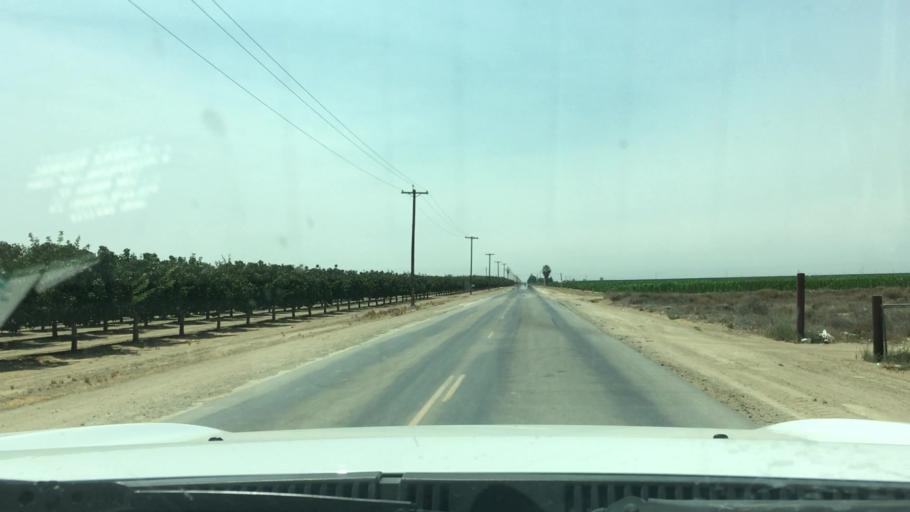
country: US
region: California
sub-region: Kern County
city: Wasco
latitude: 35.6787
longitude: -119.4374
